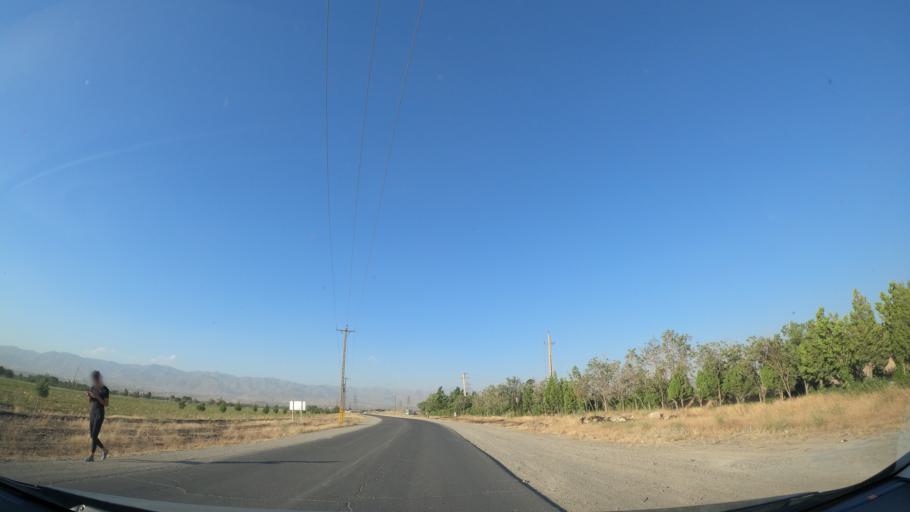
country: IR
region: Alborz
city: Hashtgerd
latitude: 35.9182
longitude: 50.7368
